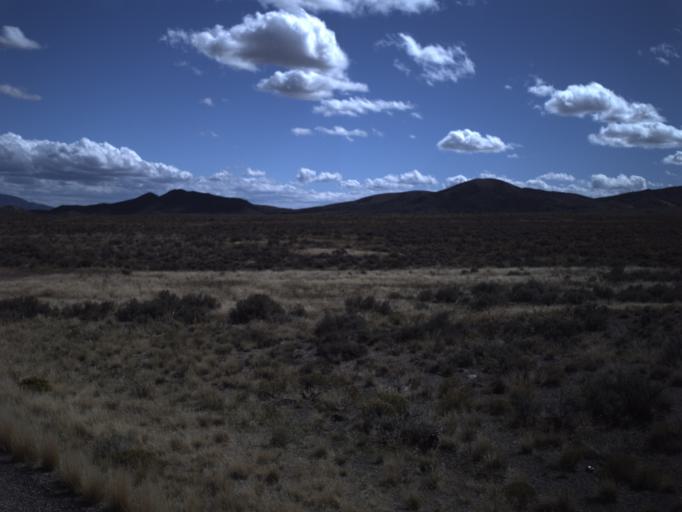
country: US
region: Utah
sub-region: Beaver County
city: Milford
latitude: 38.4364
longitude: -113.1426
